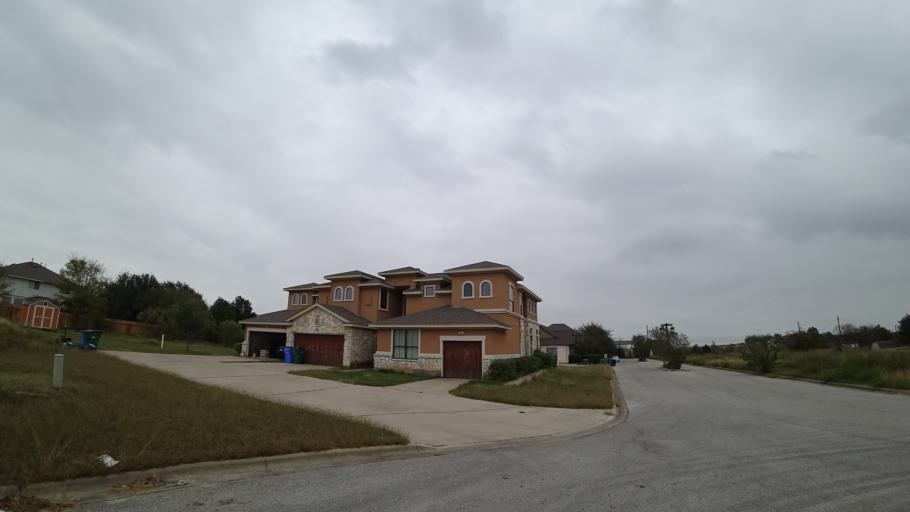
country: US
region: Texas
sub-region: Travis County
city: Pflugerville
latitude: 30.4253
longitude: -97.6184
